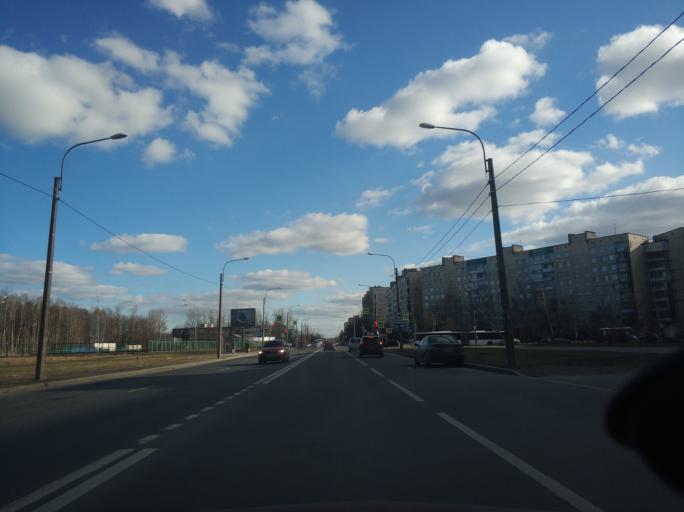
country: RU
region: St.-Petersburg
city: Krasnogvargeisky
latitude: 59.9578
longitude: 30.4928
